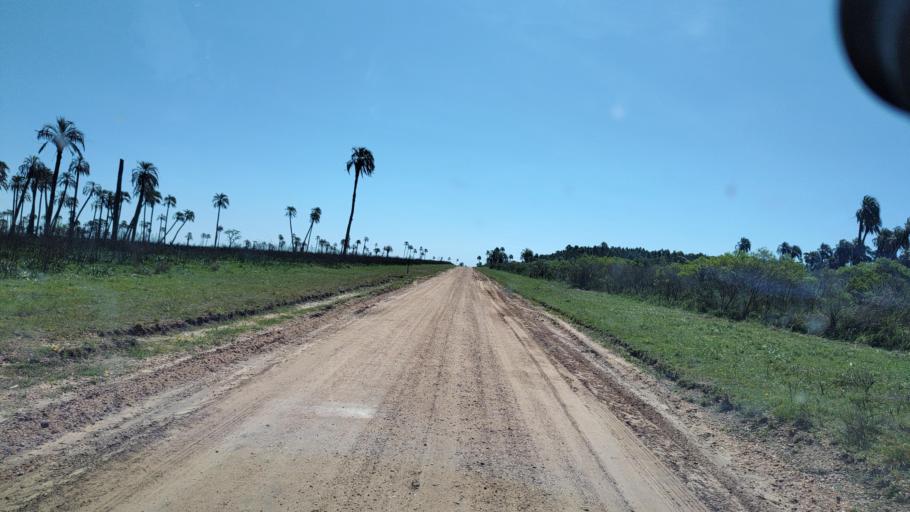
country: AR
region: Entre Rios
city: Ubajay
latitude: -31.8600
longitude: -58.2749
